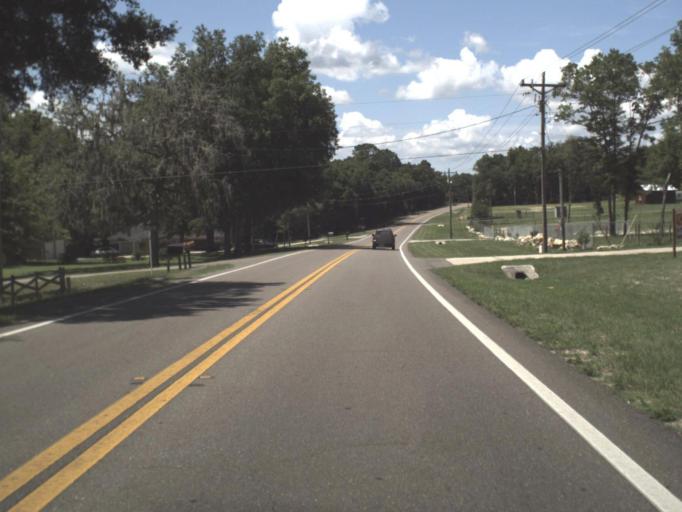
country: US
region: Florida
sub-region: Clay County
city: Keystone Heights
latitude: 29.7674
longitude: -82.0527
